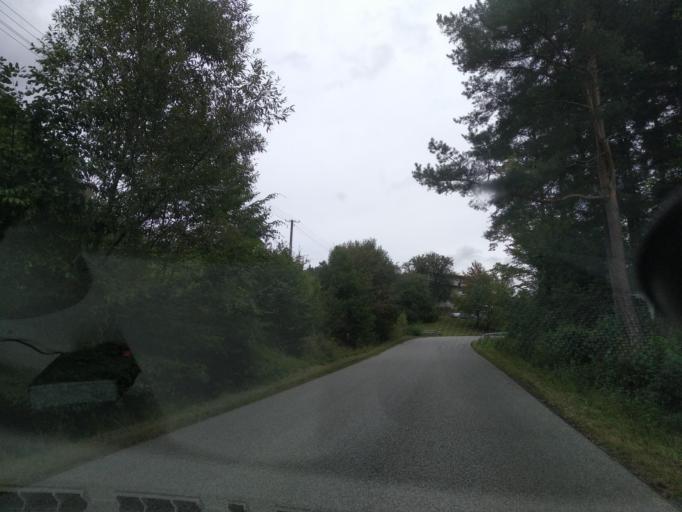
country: PL
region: Lesser Poland Voivodeship
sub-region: Powiat gorlicki
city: Sekowa
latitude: 49.6186
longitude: 21.2202
